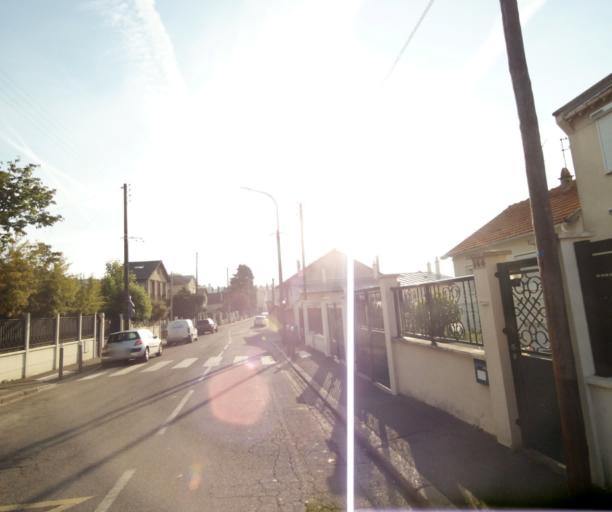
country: FR
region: Ile-de-France
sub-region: Departement du Val-d'Oise
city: Argenteuil
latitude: 48.9501
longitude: 2.2713
